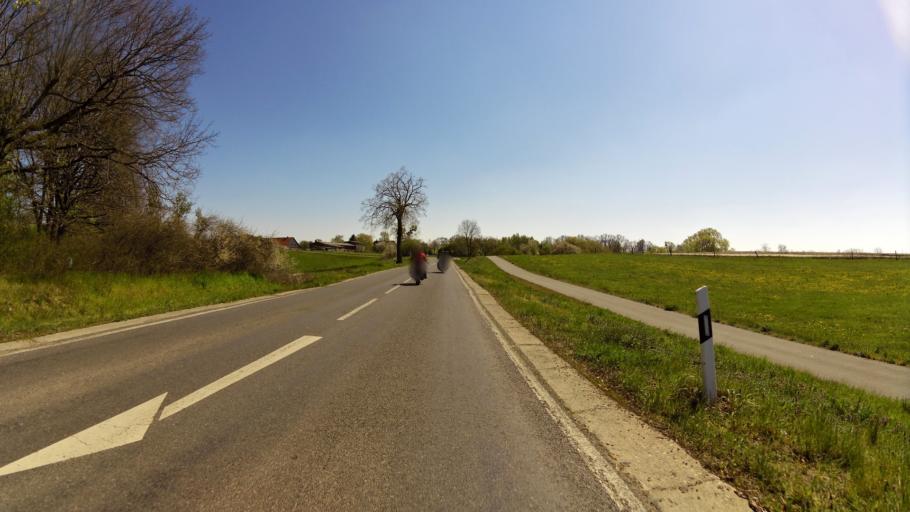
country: DE
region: Brandenburg
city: Protzel
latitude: 52.5673
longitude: 13.9637
